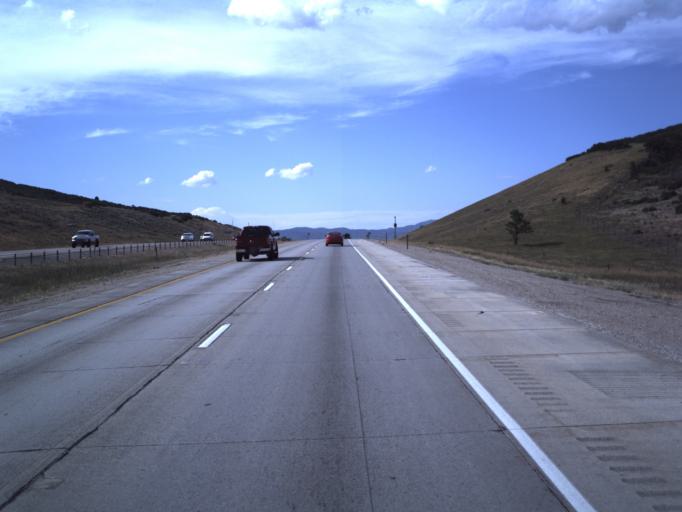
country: US
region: Utah
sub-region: Summit County
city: Park City
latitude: 40.6502
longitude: -111.4557
